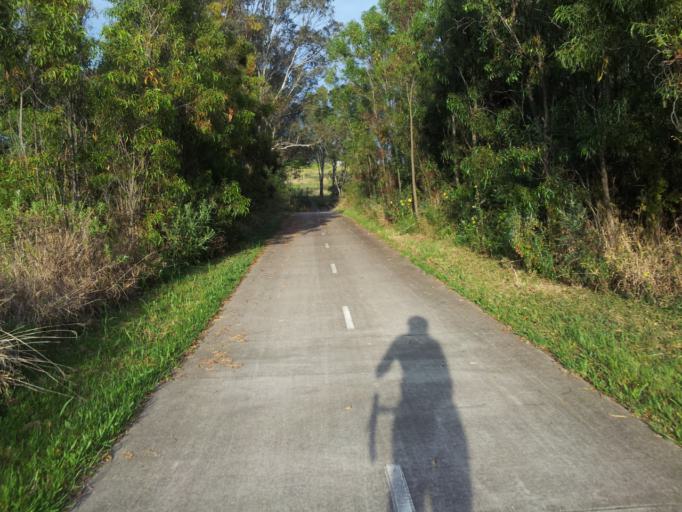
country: AU
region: New South Wales
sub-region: Fairfield
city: Horsley Park
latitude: -33.8397
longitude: 150.8746
